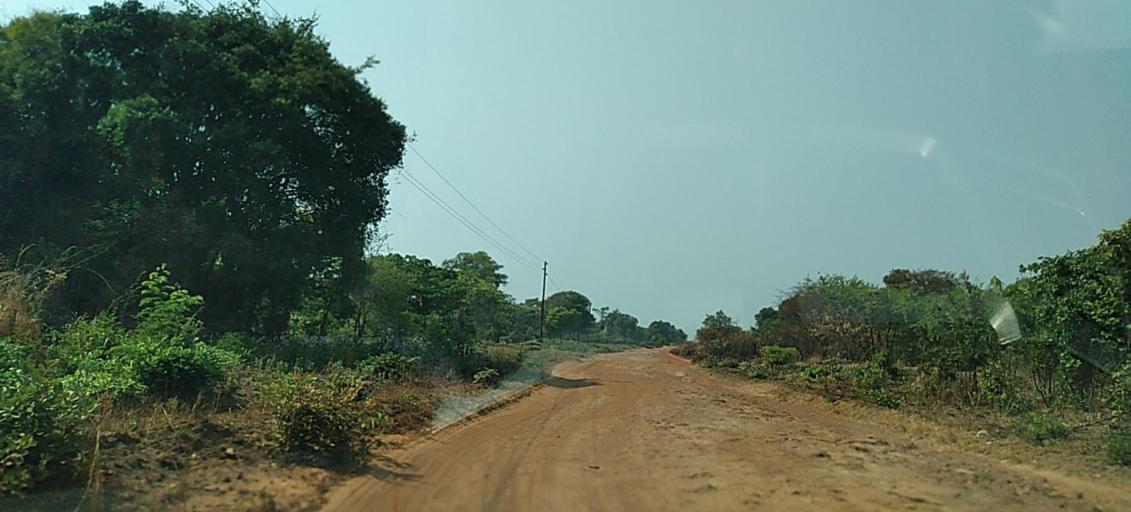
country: ZM
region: Copperbelt
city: Chingola
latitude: -12.9146
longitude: 27.3730
